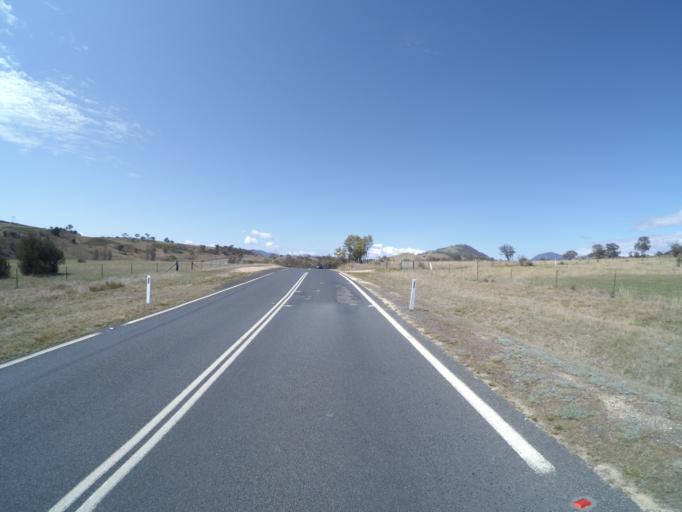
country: AU
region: Australian Capital Territory
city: Macarthur
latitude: -35.4595
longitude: 149.0174
